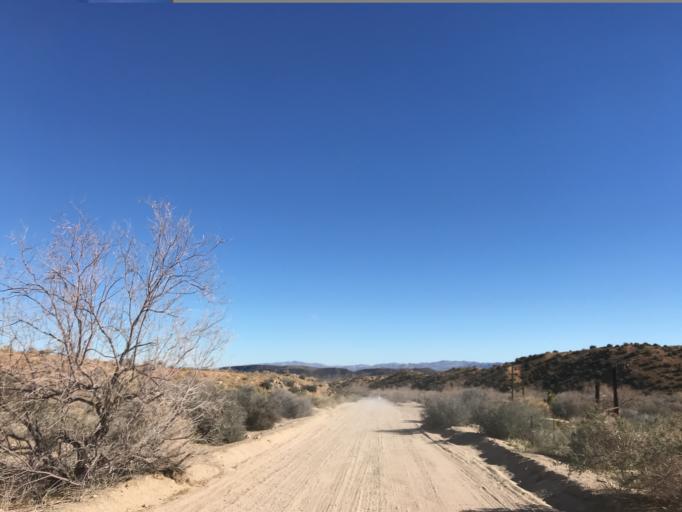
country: US
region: California
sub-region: San Bernardino County
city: Morongo Valley
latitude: 34.1983
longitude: -116.5687
